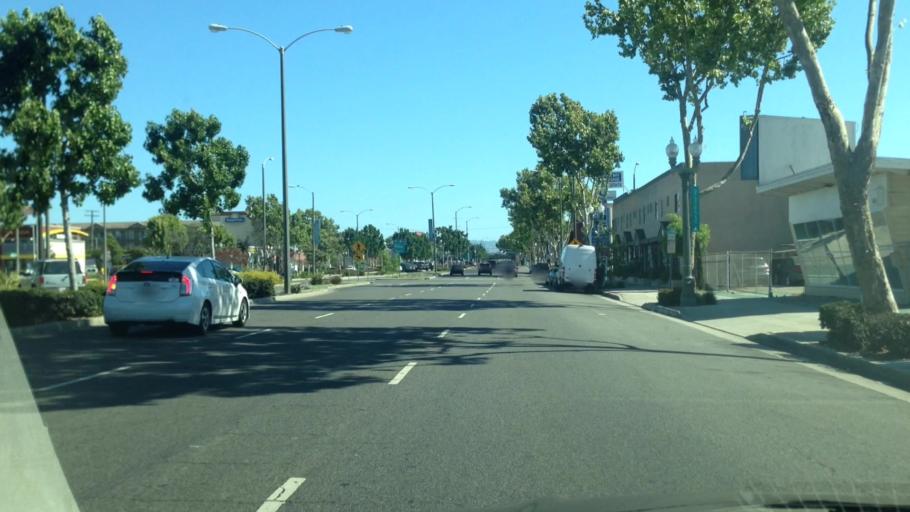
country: US
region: California
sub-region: Los Angeles County
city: Lawndale
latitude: 33.8906
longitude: -118.3528
